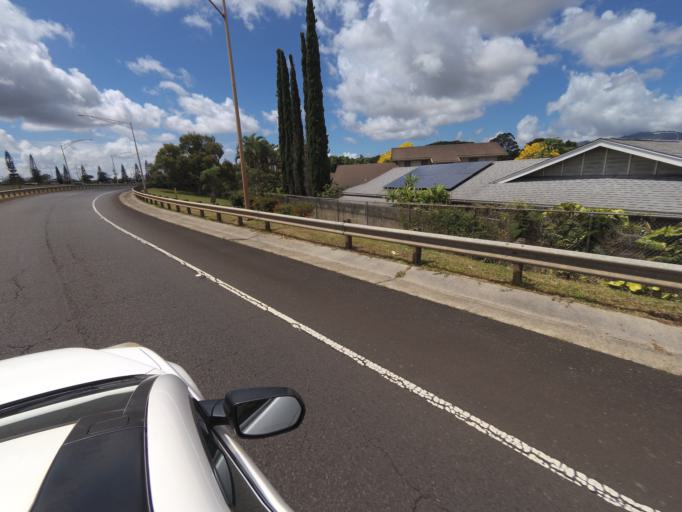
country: US
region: Hawaii
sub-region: Honolulu County
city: Waipi'o Acres
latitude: 21.4668
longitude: -158.0060
